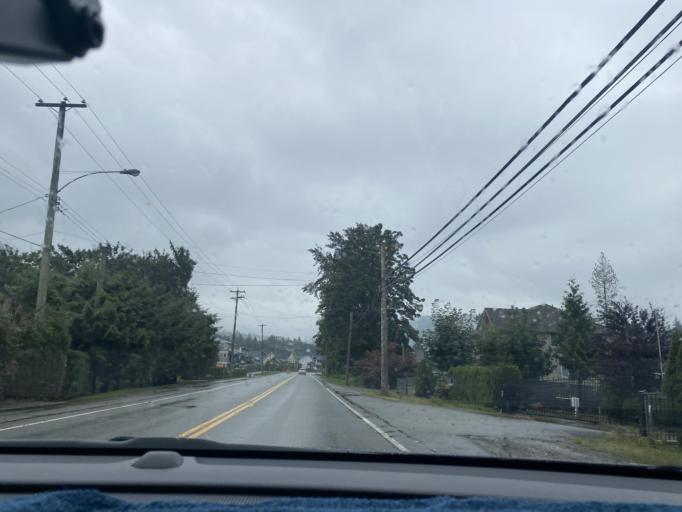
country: CA
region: British Columbia
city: Agassiz
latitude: 49.2948
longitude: -121.7834
